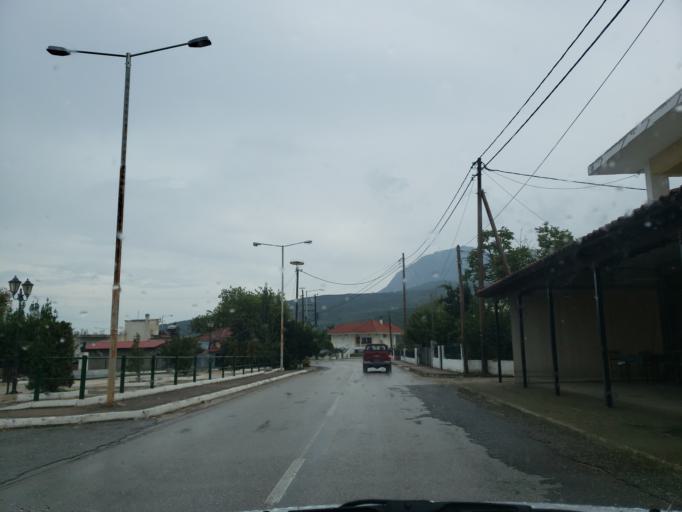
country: GR
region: Central Greece
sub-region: Nomos Fthiotidos
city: Anthili
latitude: 38.7993
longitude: 22.4683
